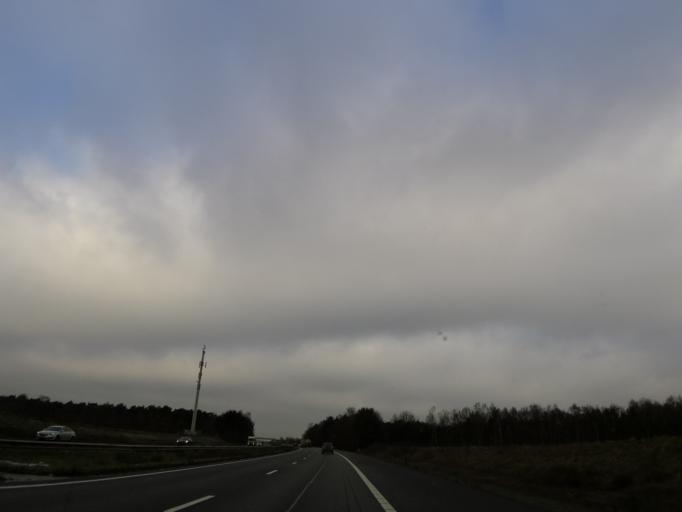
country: NL
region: Limburg
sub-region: Gemeente Leudal
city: Kelpen-Oler
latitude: 51.2454
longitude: 5.7837
